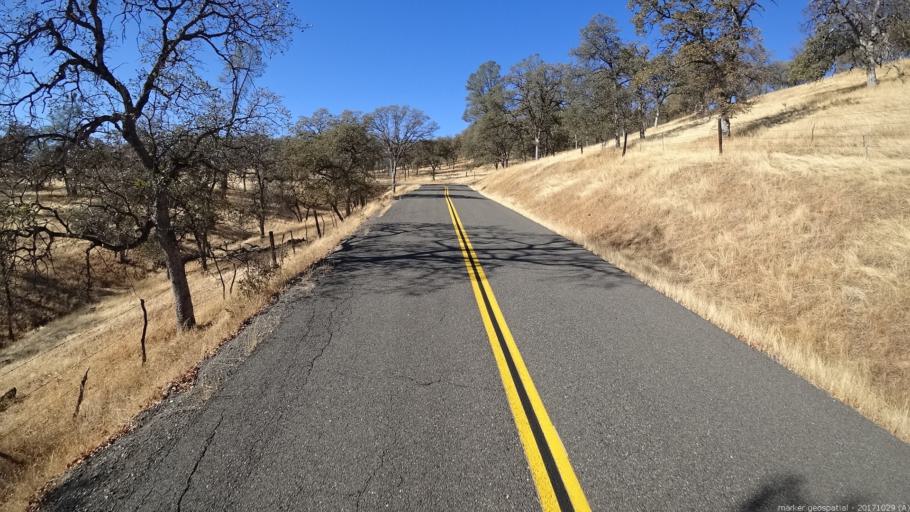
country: US
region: California
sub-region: Trinity County
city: Lewiston
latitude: 40.3881
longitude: -122.8052
